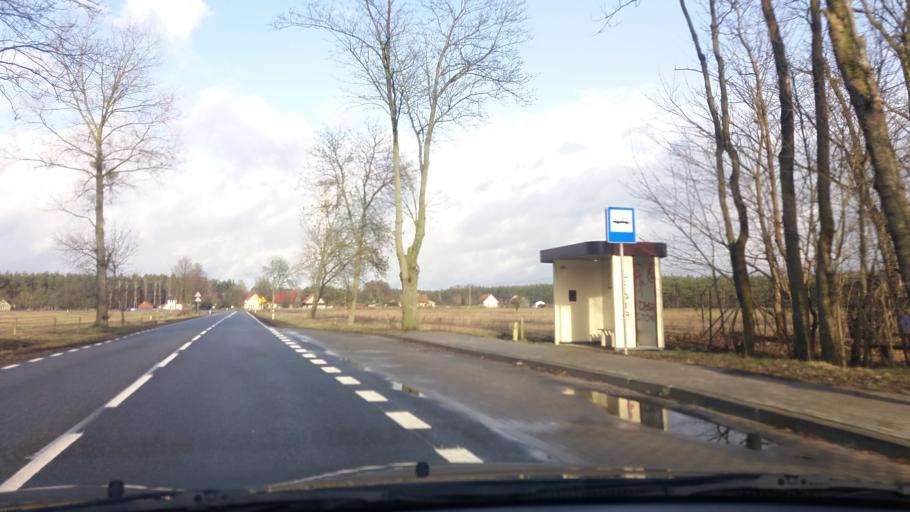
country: PL
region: Masovian Voivodeship
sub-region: Powiat przasnyski
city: Chorzele
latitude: 53.2904
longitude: 20.9136
